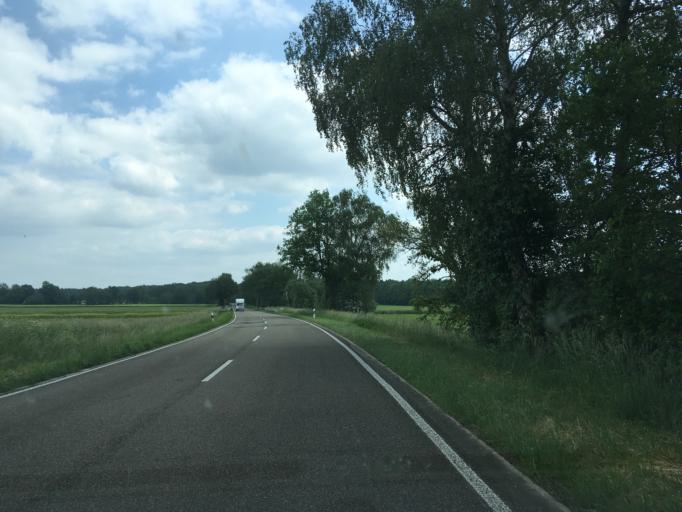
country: DE
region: North Rhine-Westphalia
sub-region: Regierungsbezirk Munster
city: Raesfeld
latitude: 51.7804
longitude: 6.7815
